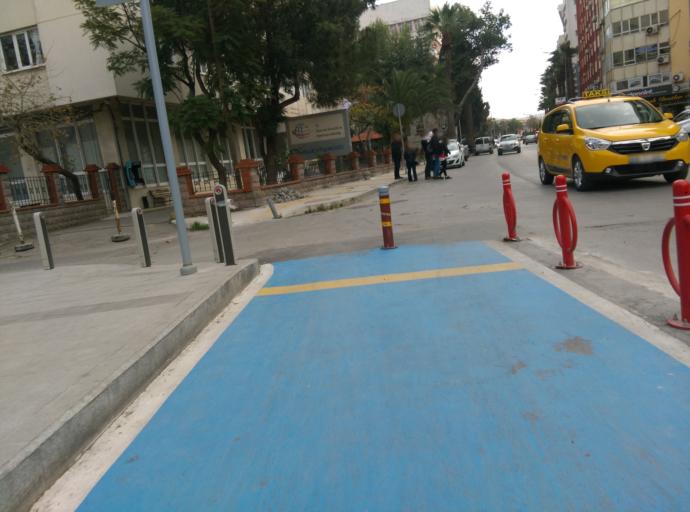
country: TR
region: Izmir
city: Izmir
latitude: 38.4413
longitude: 27.1464
